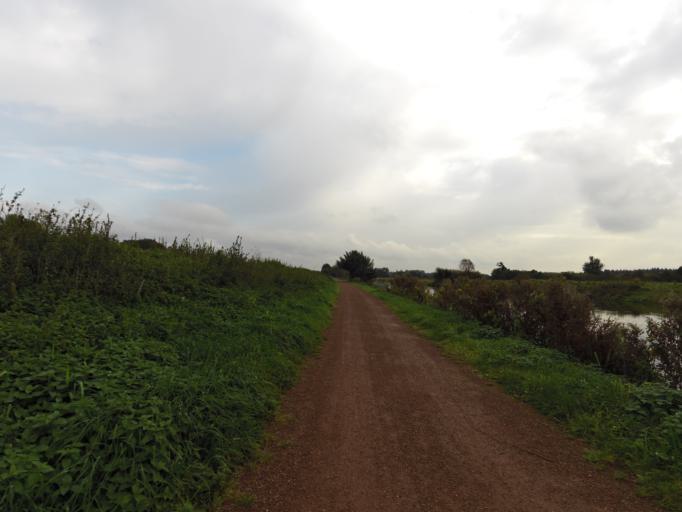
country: DE
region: North Rhine-Westphalia
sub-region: Regierungsbezirk Munster
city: Isselburg
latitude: 51.8519
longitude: 6.4804
